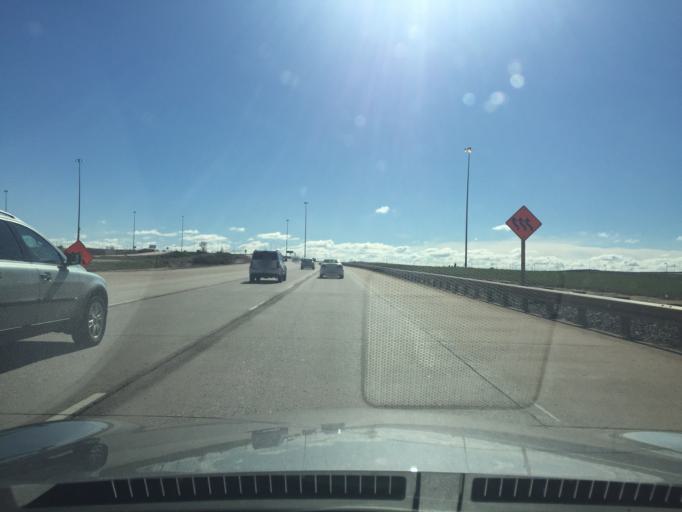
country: US
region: Colorado
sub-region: Adams County
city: Aurora
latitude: 39.8332
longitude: -104.7225
